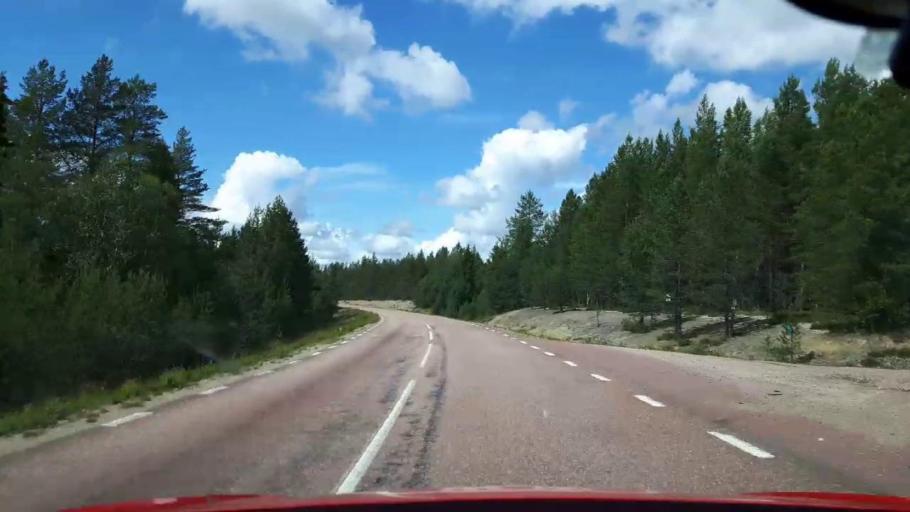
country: SE
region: Dalarna
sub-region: Alvdalens Kommun
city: AElvdalen
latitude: 61.8053
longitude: 13.6514
